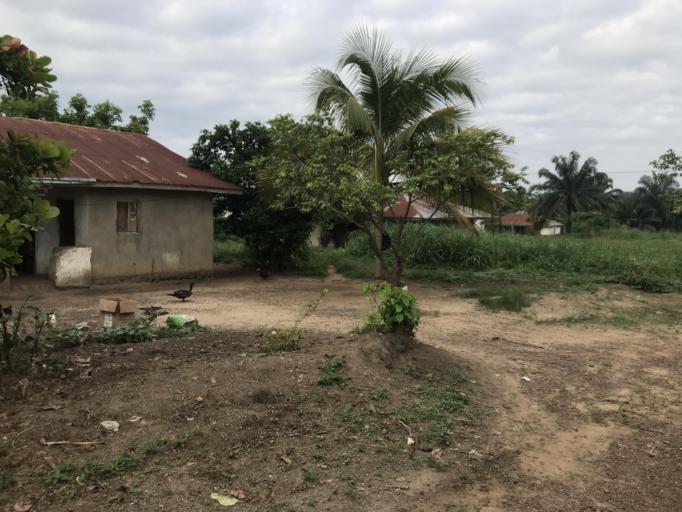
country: SL
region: Eastern Province
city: Pendembu
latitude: 8.0892
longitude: -10.6921
